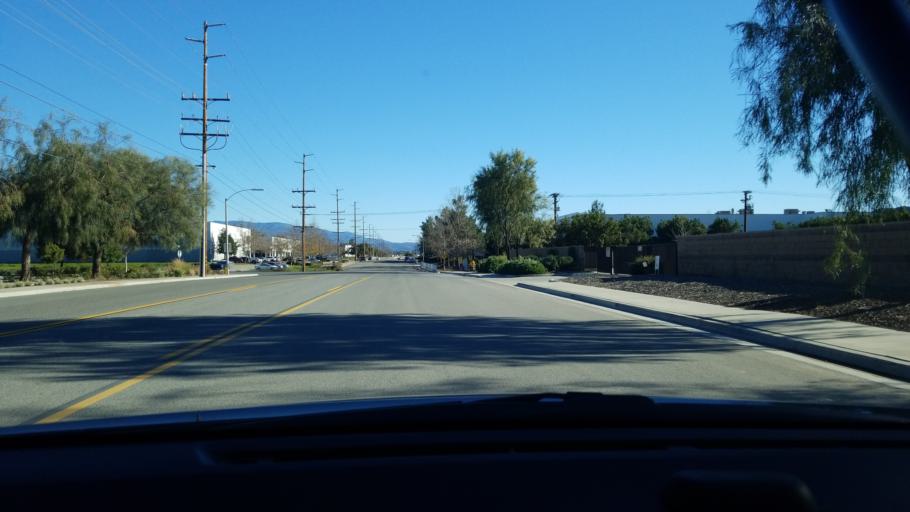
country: US
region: California
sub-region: Riverside County
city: Murrieta
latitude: 33.5326
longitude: -117.1854
